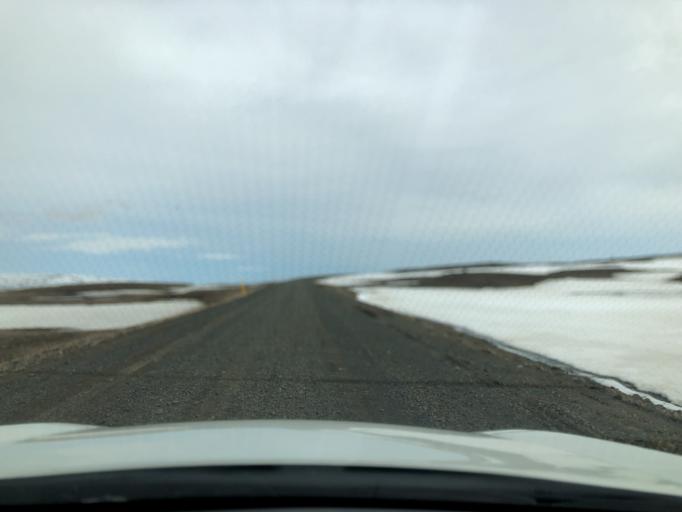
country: IS
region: East
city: Egilsstadir
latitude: 65.3074
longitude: -15.3881
